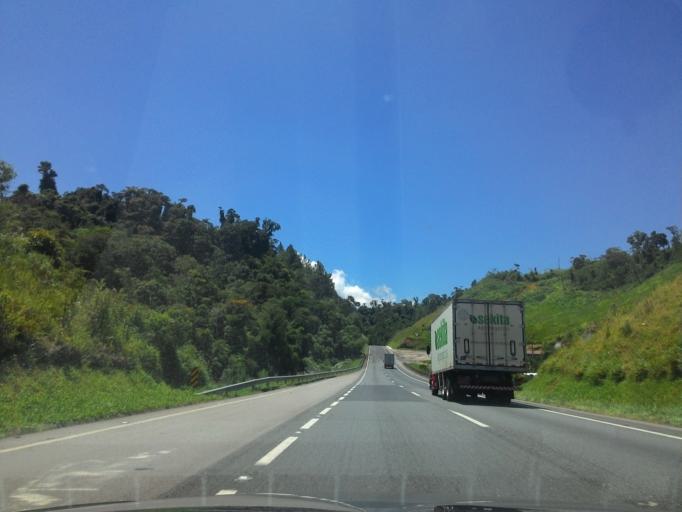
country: BR
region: Parana
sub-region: Antonina
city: Antonina
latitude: -25.0661
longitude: -48.5710
